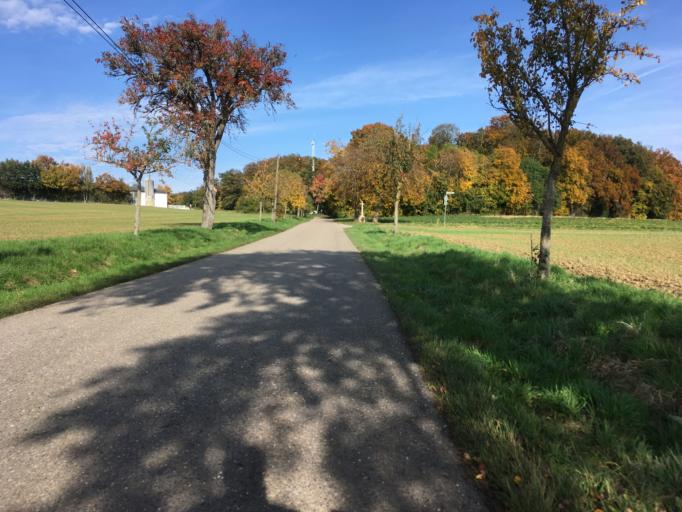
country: DE
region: Baden-Wuerttemberg
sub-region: Regierungsbezirk Stuttgart
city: Siegelsbach
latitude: 49.2625
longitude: 9.0414
